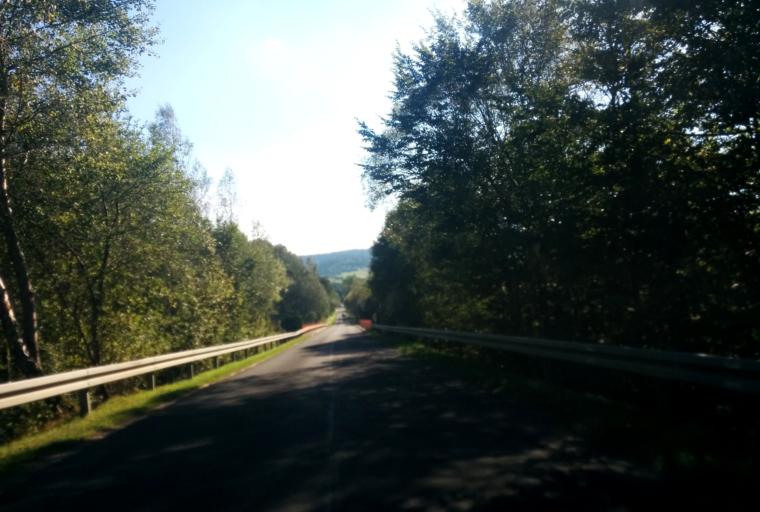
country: PL
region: Subcarpathian Voivodeship
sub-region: Powiat leski
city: Polanczyk
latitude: 49.3194
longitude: 22.4144
